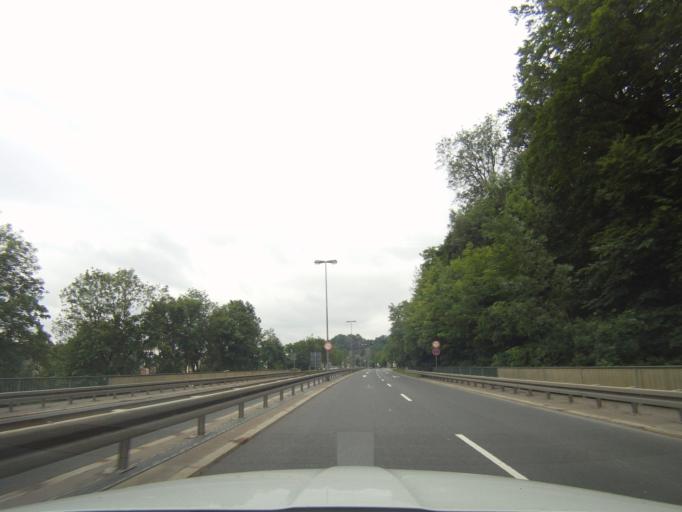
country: DE
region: Bavaria
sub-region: Upper Franconia
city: Coburg
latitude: 50.2675
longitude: 10.9558
